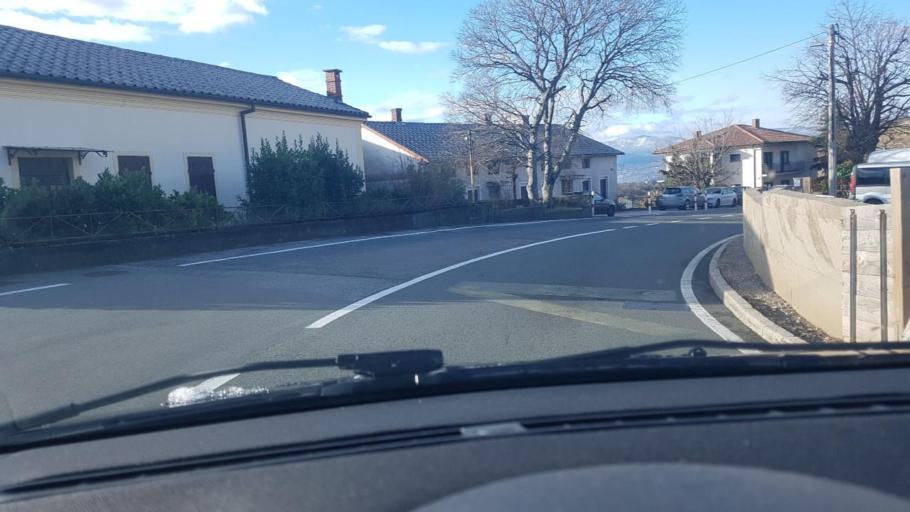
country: HR
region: Primorsko-Goranska
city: Cavle
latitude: 45.3487
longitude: 14.4818
